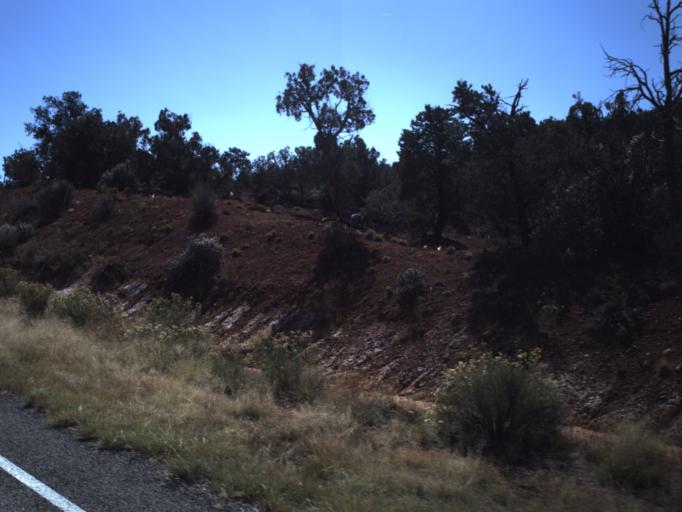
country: US
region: Utah
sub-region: San Juan County
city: Blanding
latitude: 37.5653
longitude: -110.0294
